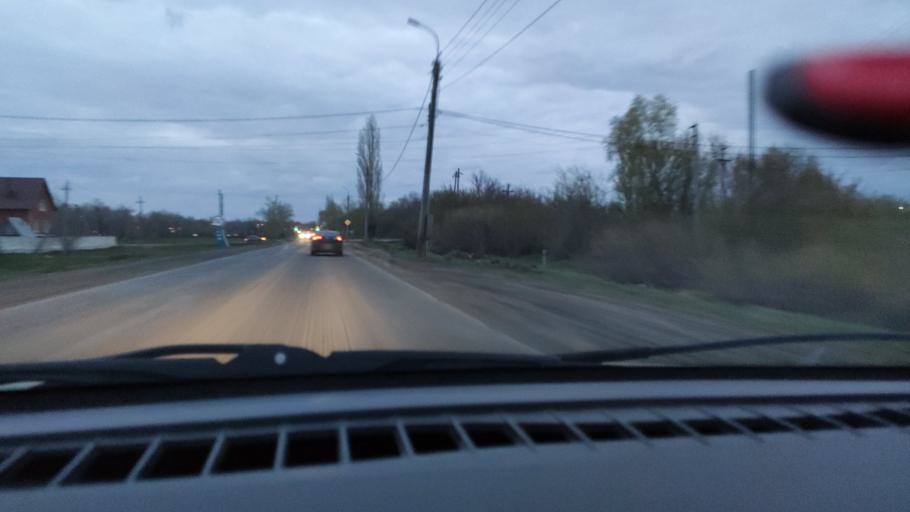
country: RU
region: Orenburg
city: Tatarskaya Kargala
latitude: 51.8629
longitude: 55.1370
